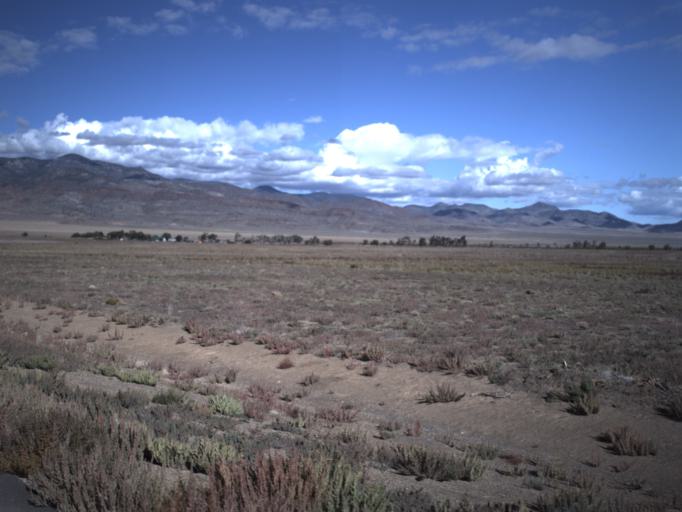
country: US
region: Utah
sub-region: Beaver County
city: Milford
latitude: 38.4744
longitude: -113.4188
